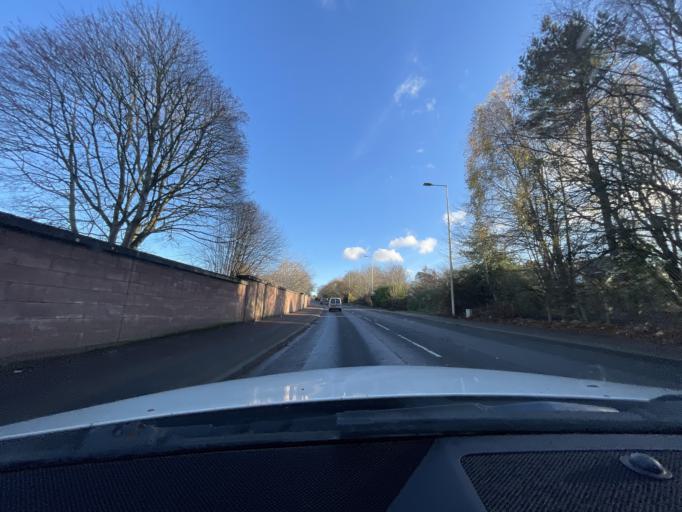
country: GB
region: Scotland
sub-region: Highland
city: Inverness
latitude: 57.4498
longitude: -4.2488
